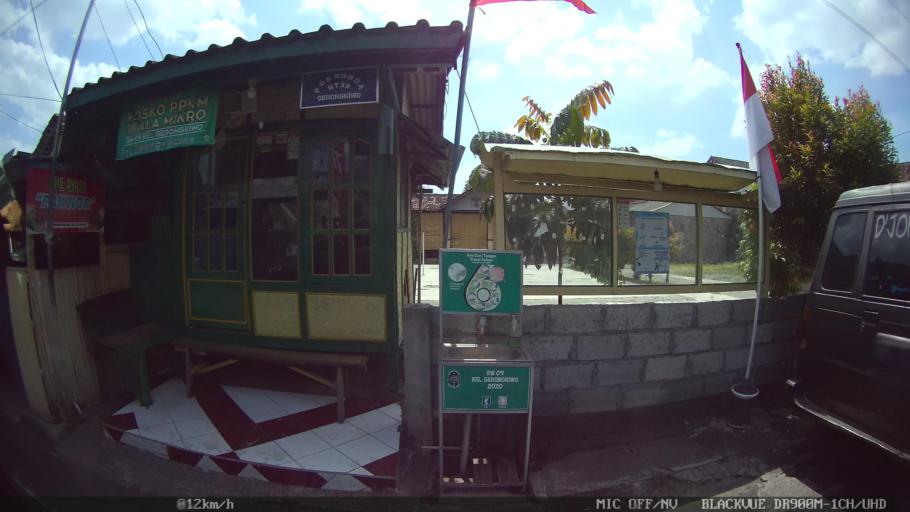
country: ID
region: Daerah Istimewa Yogyakarta
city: Kasihan
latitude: -7.8135
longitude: 110.3538
